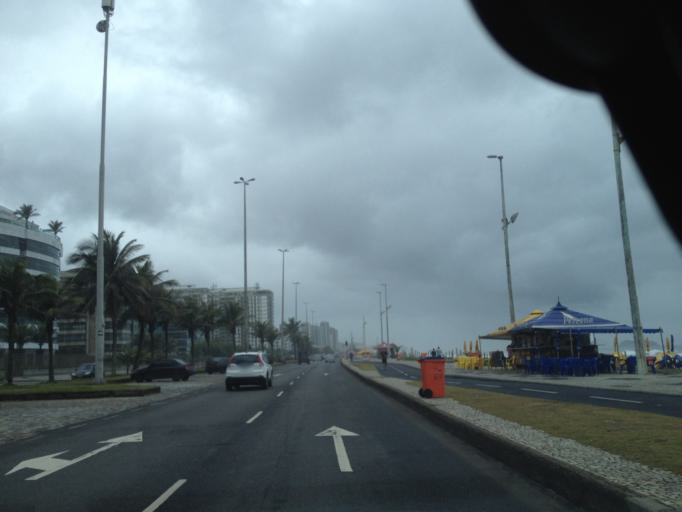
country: BR
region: Rio de Janeiro
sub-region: Rio De Janeiro
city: Rio de Janeiro
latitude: -23.0104
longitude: -43.3498
